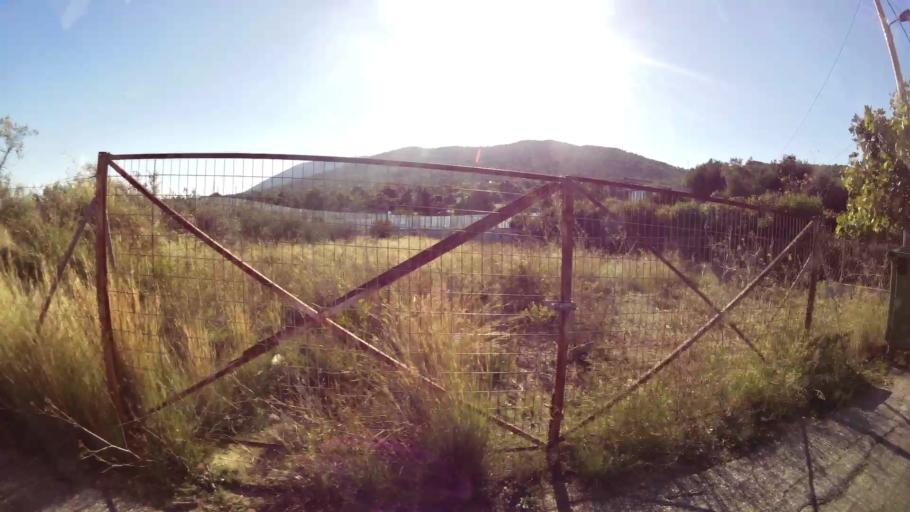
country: GR
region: Attica
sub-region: Nomarchia Anatolikis Attikis
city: Leondarion
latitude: 37.9990
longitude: 23.8447
